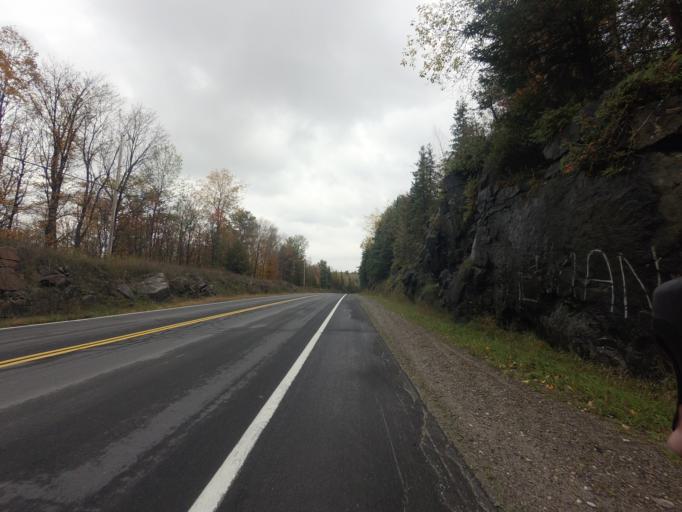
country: CA
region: Ontario
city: Perth
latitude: 45.1140
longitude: -76.4862
